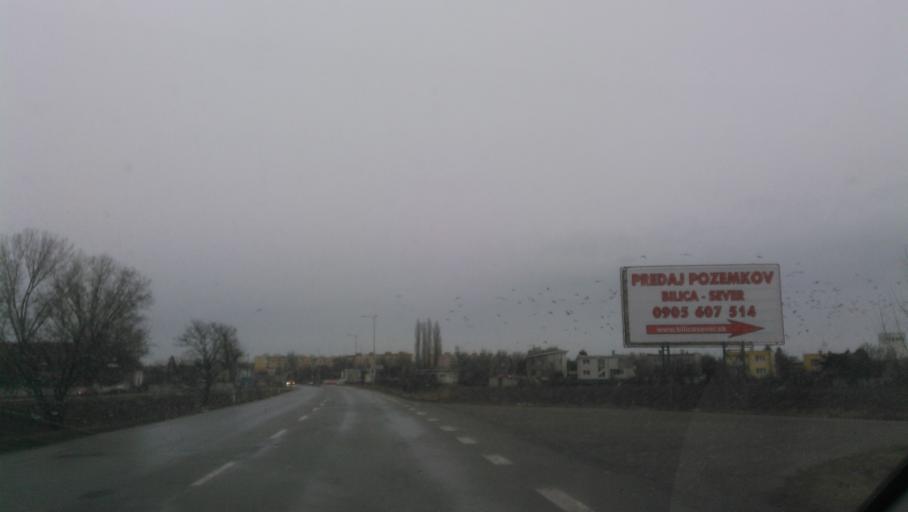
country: SK
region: Nitriansky
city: Sellye
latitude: 48.1573
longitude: 17.8598
